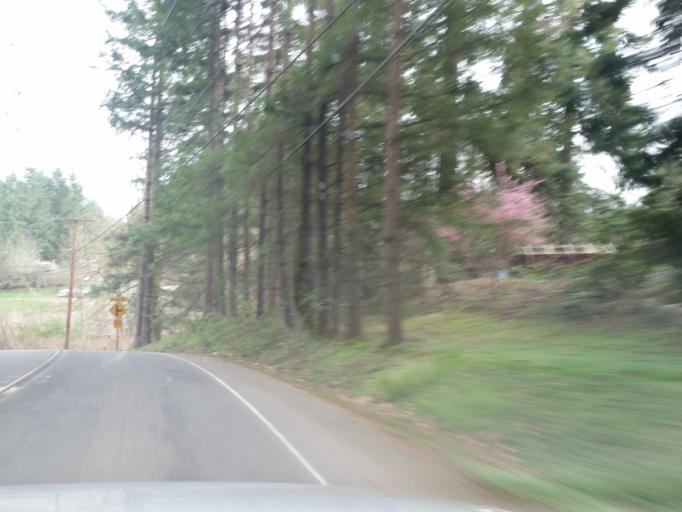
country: US
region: Washington
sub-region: King County
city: Cottage Lake
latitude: 47.7475
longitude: -122.1070
